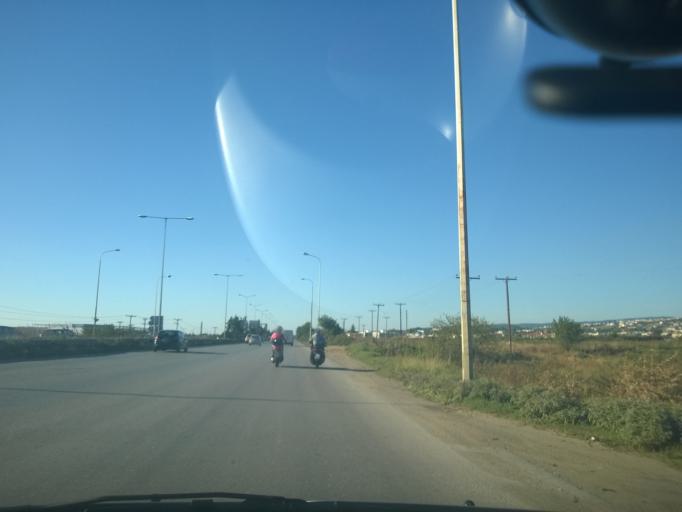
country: GR
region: Central Macedonia
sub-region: Nomos Thessalonikis
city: Thermi
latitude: 40.5408
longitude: 23.0080
